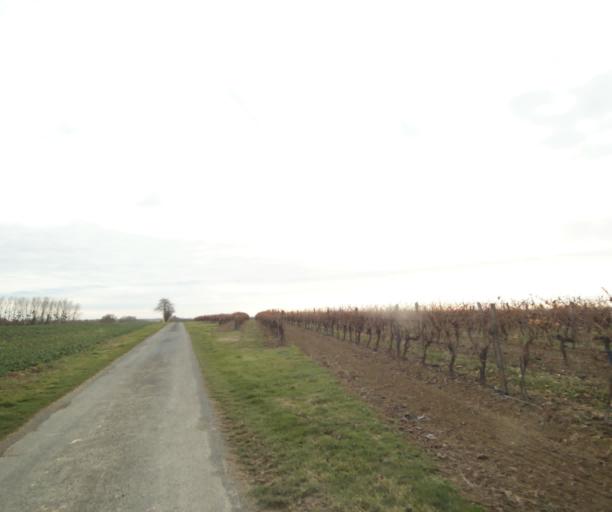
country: FR
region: Poitou-Charentes
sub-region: Departement de la Charente-Maritime
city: Corme-Royal
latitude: 45.7436
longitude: -0.7950
